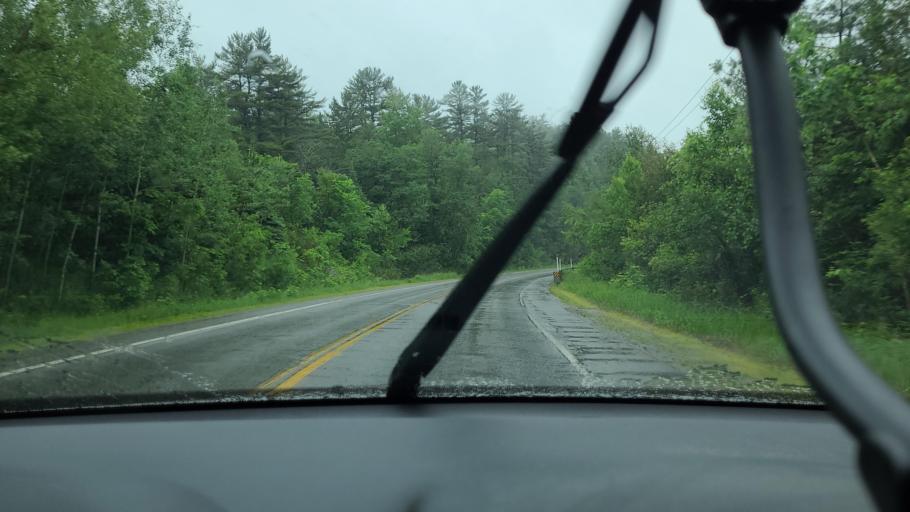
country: CA
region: Quebec
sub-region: Outaouais
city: Papineauville
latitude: 45.6737
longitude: -75.0255
